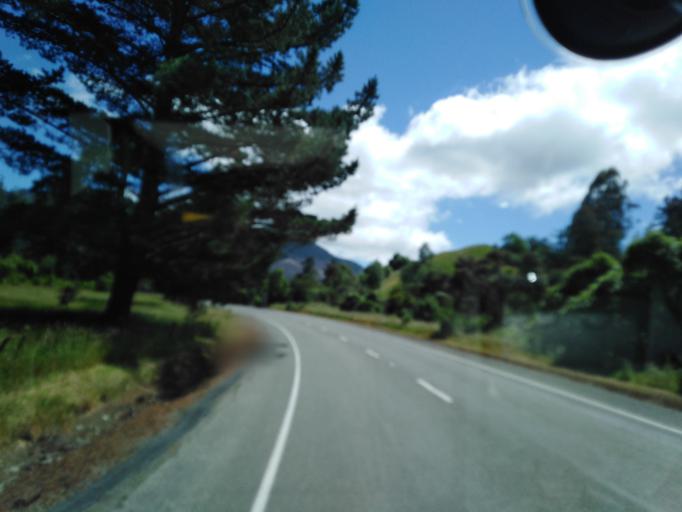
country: NZ
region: Nelson
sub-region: Nelson City
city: Nelson
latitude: -41.2205
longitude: 173.3979
